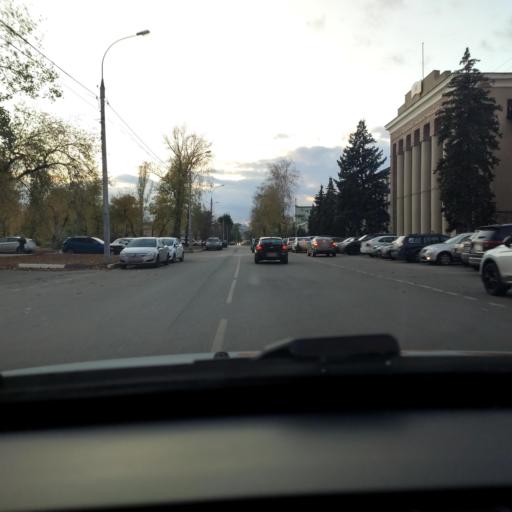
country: RU
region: Voronezj
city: Voronezh
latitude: 51.6364
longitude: 39.2509
